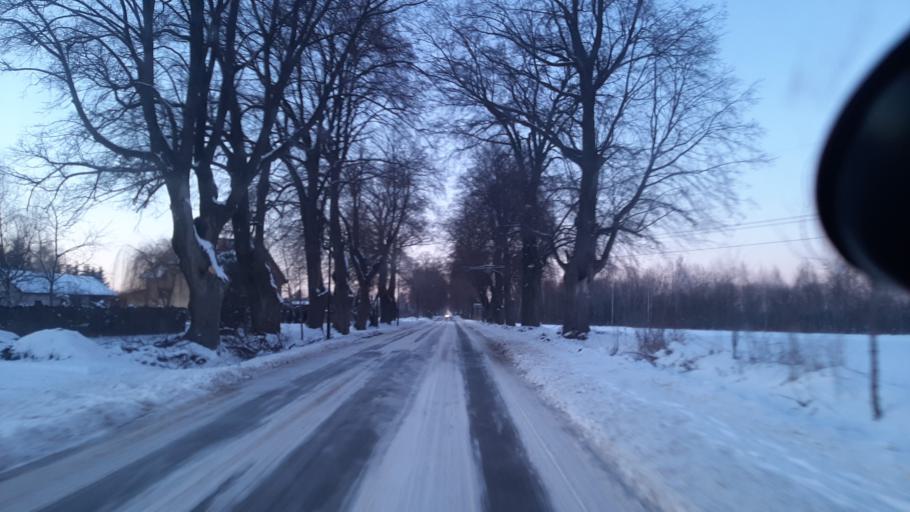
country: PL
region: Lublin Voivodeship
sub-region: Powiat lubelski
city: Lublin
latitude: 51.3294
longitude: 22.5570
